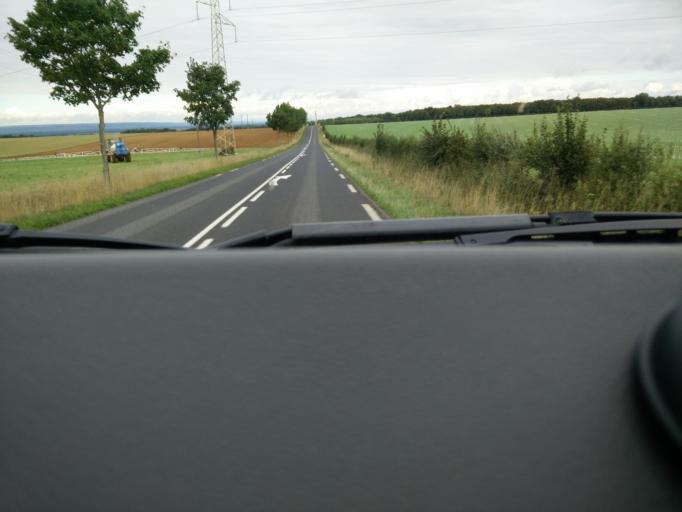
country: FR
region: Lorraine
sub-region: Departement de Meurthe-et-Moselle
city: Montauville
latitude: 48.9268
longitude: 5.9052
